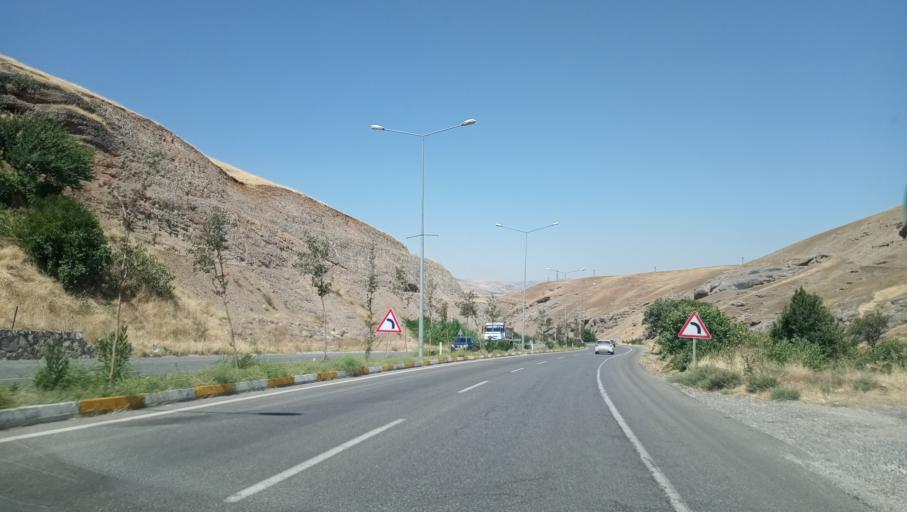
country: TR
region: Siirt
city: Civankan
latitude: 37.9480
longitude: 41.8740
